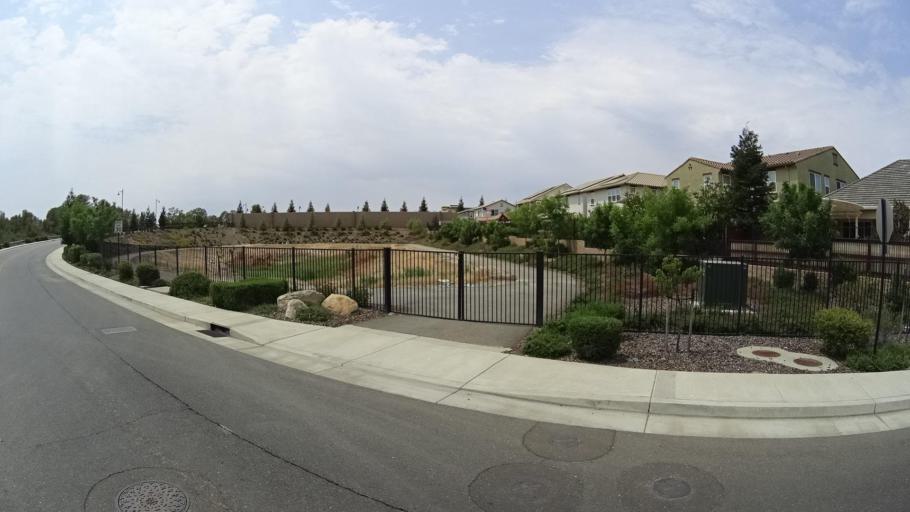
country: US
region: California
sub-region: Placer County
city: Loomis
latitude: 38.8002
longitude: -121.1992
